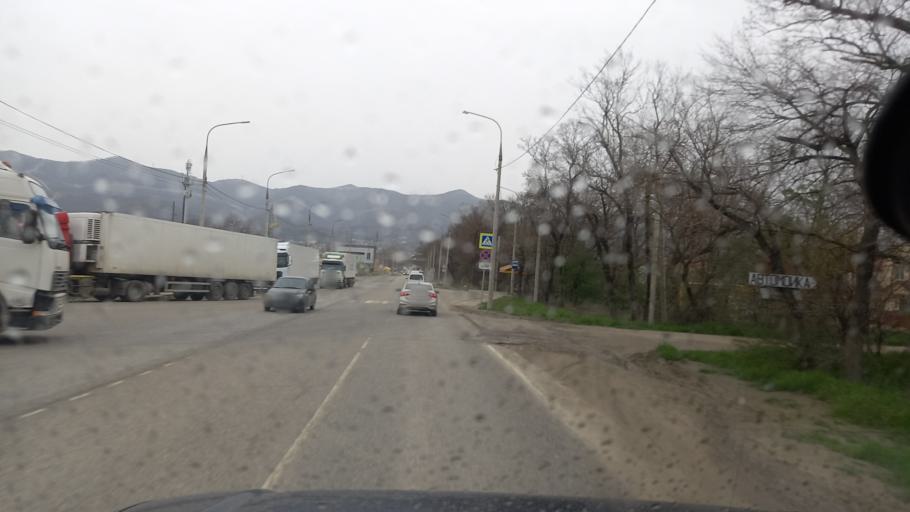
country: RU
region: Krasnodarskiy
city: Gayduk
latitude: 44.7579
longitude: 37.7099
